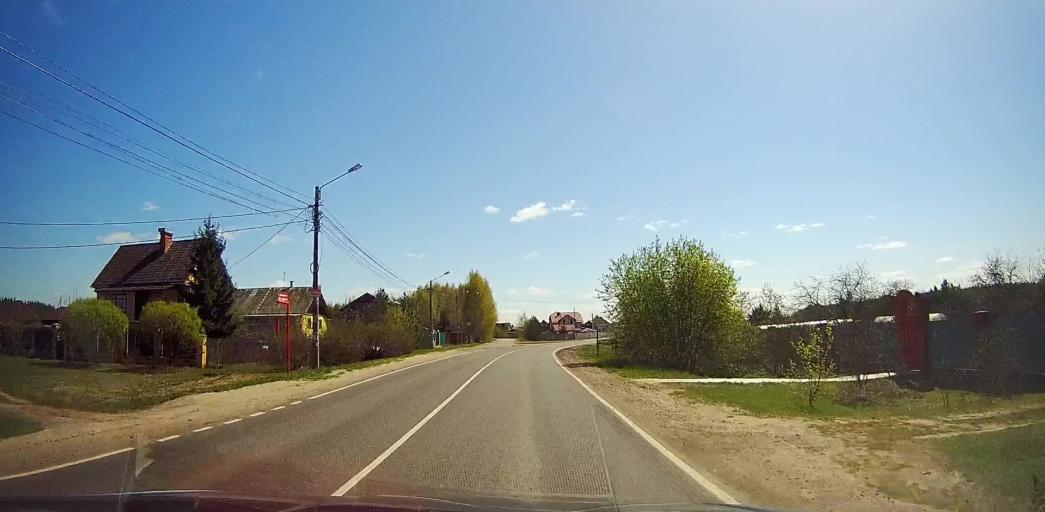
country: RU
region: Moskovskaya
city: Rechitsy
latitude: 55.5356
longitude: 38.4271
